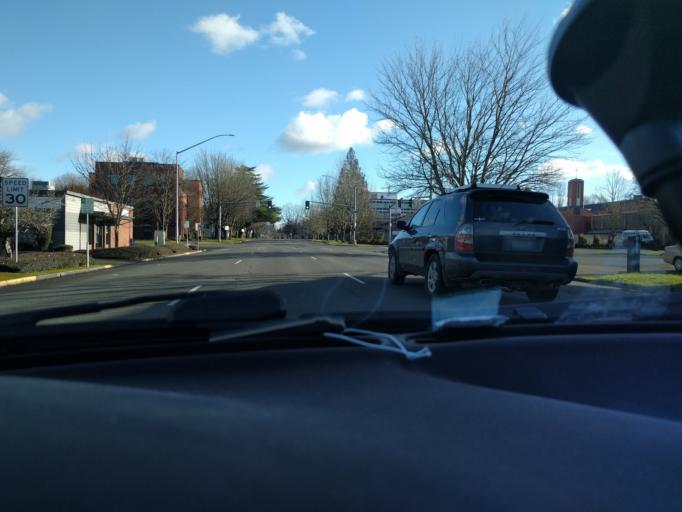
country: US
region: Oregon
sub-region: Marion County
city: Salem
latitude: 44.9424
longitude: -123.0331
